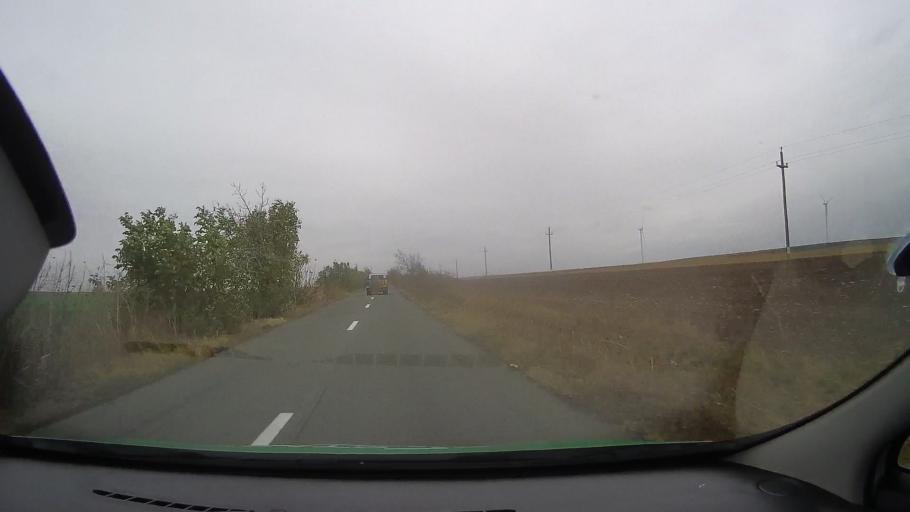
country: RO
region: Constanta
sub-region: Comuna Targusor
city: Targusor
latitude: 44.4752
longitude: 28.3811
